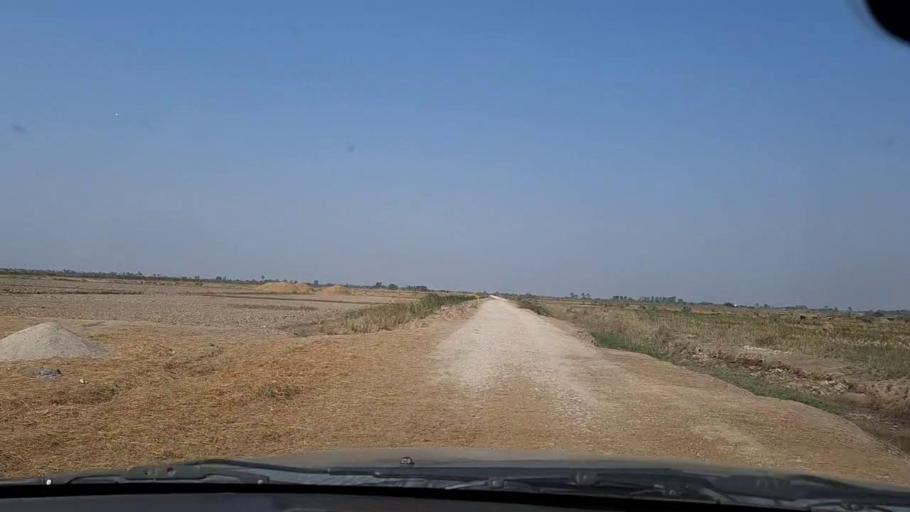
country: PK
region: Sindh
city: Mirpur Sakro
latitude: 24.3666
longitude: 67.6830
